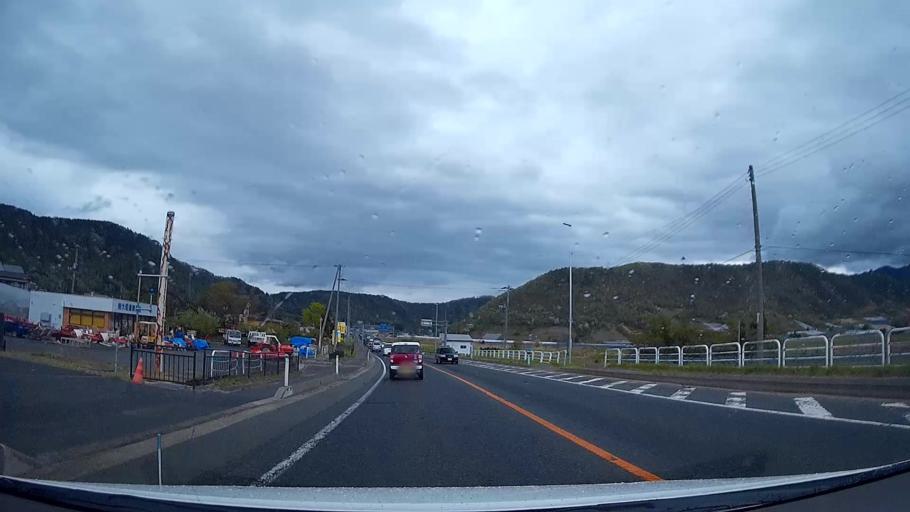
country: JP
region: Yamagata
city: Takahata
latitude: 38.0780
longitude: 140.1842
